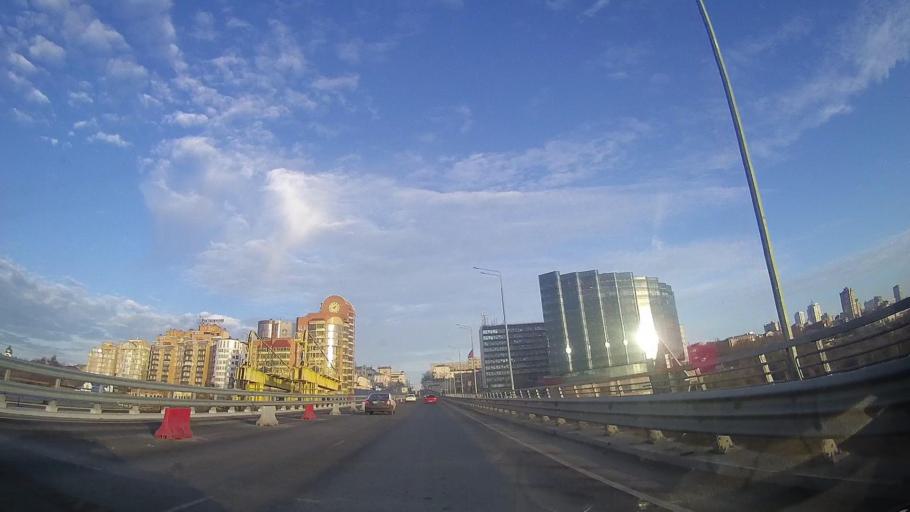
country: RU
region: Rostov
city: Rostov-na-Donu
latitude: 47.2149
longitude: 39.7232
